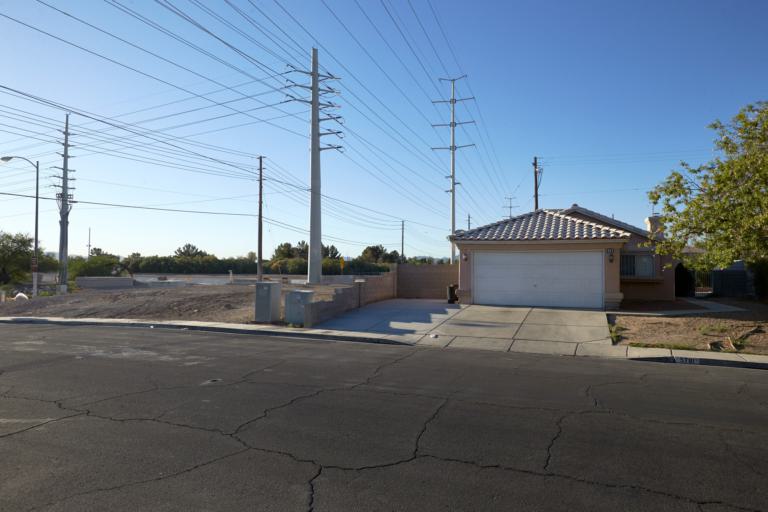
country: US
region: Nevada
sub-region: Clark County
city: Winchester
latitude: 36.1407
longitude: -115.0478
